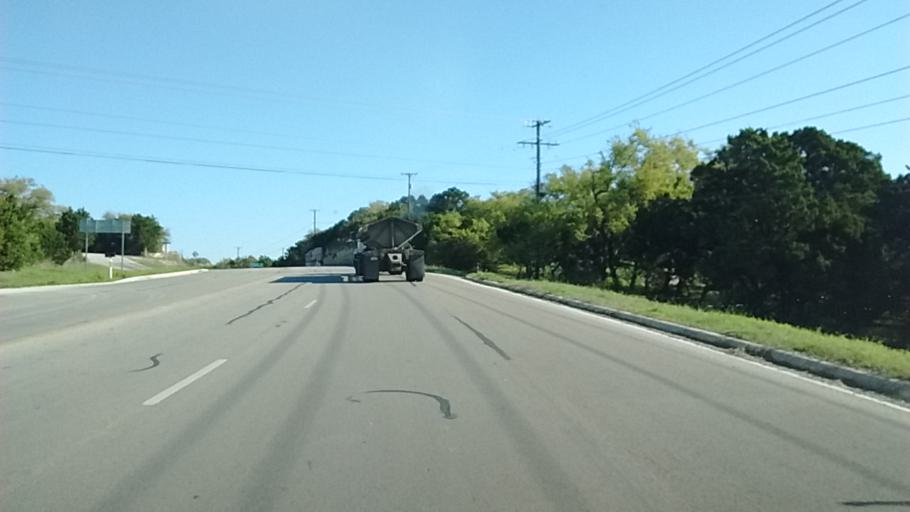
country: US
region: Texas
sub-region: Comal County
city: New Braunfels
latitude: 29.7394
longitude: -98.2028
